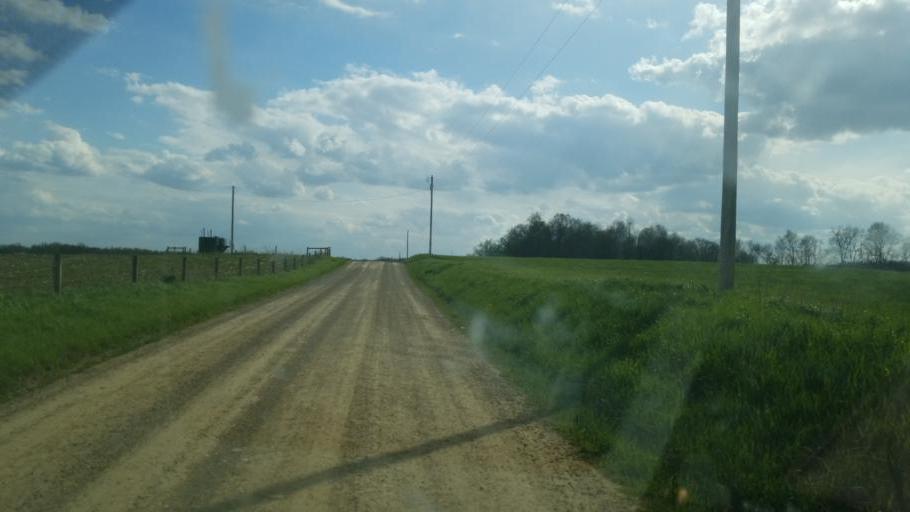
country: US
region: Ohio
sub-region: Knox County
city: Gambier
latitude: 40.4775
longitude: -82.4207
